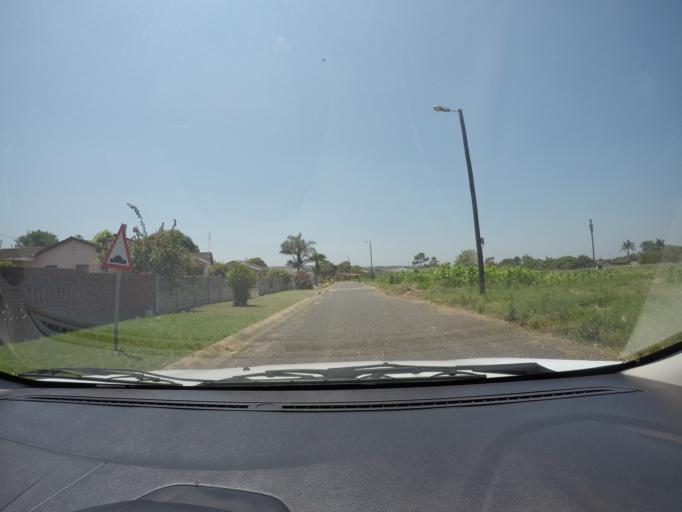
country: ZA
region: KwaZulu-Natal
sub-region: uThungulu District Municipality
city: eSikhawini
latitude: -28.8918
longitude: 31.8839
